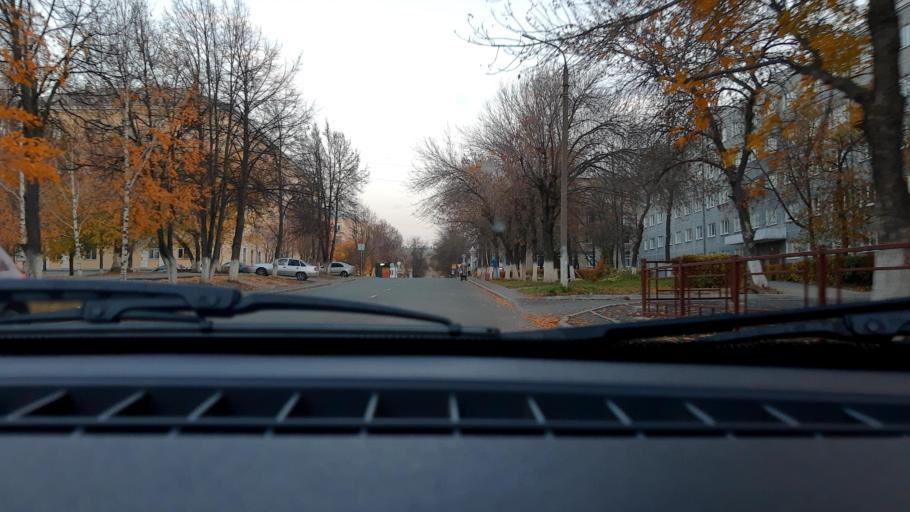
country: RU
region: Bashkortostan
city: Ufa
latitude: 54.8164
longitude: 56.0605
